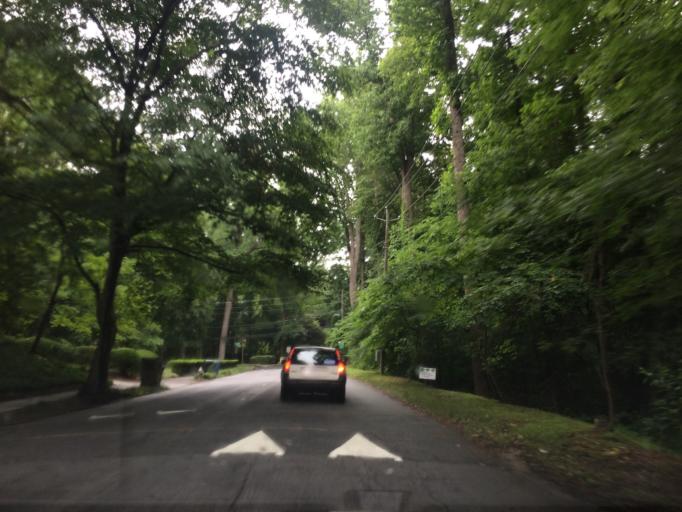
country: US
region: Georgia
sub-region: DeKalb County
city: Druid Hills
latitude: 33.7783
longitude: -84.3344
